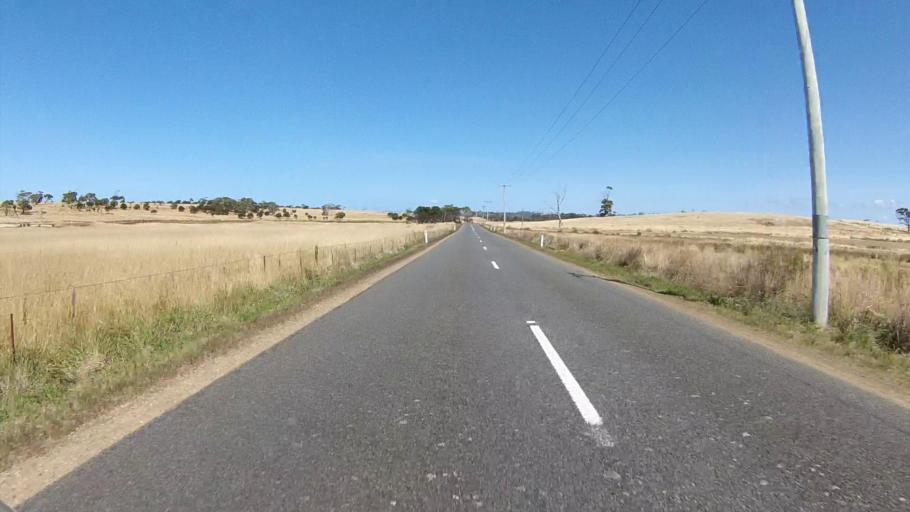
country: AU
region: Tasmania
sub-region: Sorell
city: Sorell
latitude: -42.2735
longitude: 148.0041
